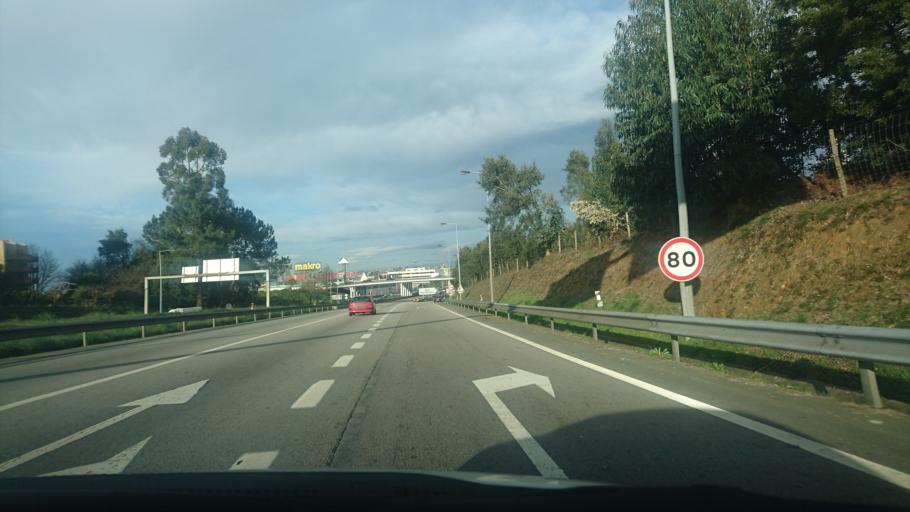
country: PT
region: Porto
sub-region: Vila Nova de Gaia
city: Vila Nova de Gaia
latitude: 41.1176
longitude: -8.6252
